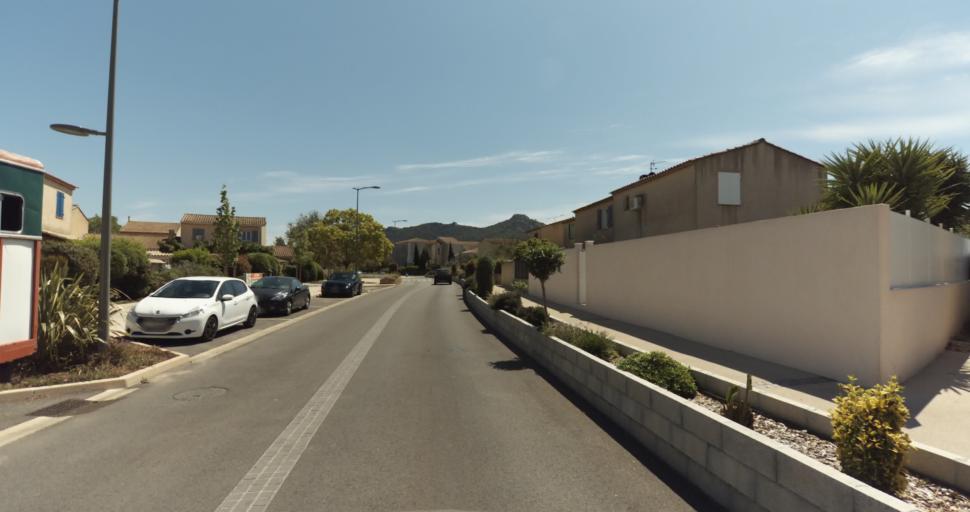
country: FR
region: Provence-Alpes-Cote d'Azur
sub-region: Departement du Var
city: La Crau
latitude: 43.1442
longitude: 6.0759
